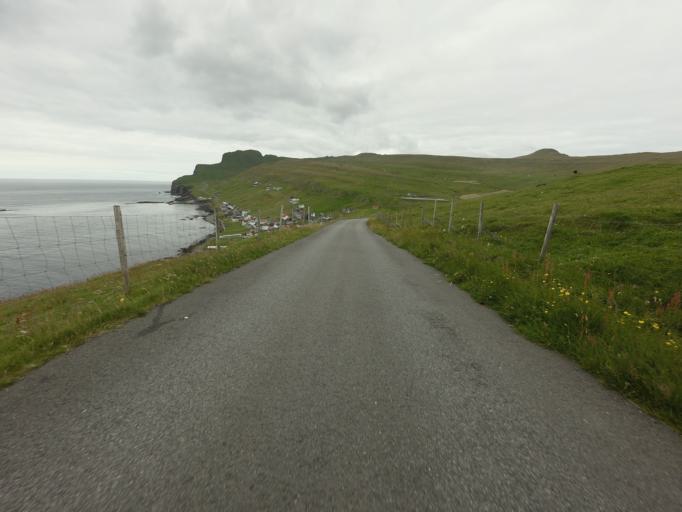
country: FO
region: Suduroy
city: Vagur
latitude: 61.4006
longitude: -6.7054
